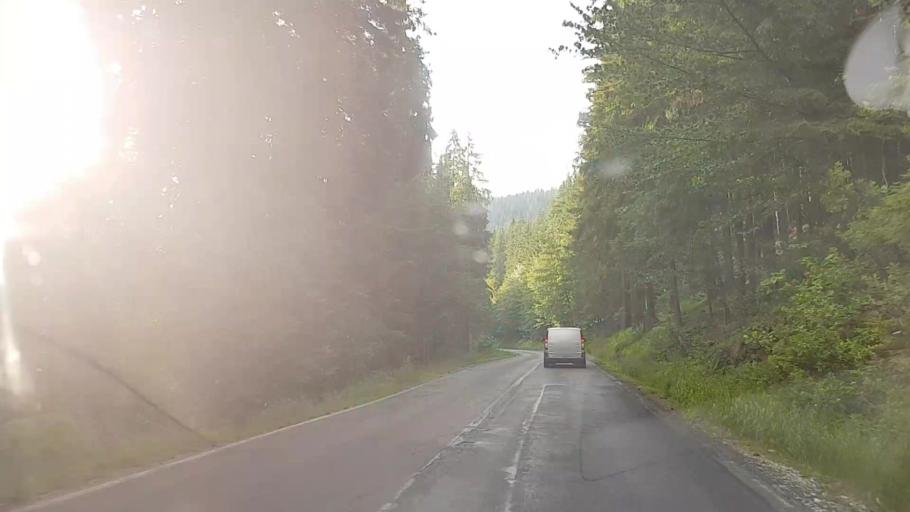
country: RO
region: Harghita
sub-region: Comuna Varsag
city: Varsag
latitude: 46.6634
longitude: 25.3156
